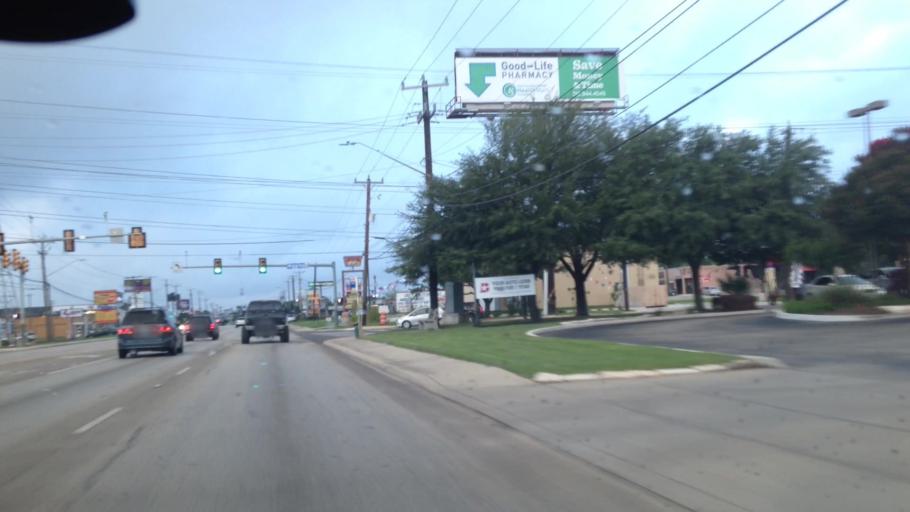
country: US
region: Texas
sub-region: Bexar County
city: Windcrest
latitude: 29.5637
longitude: -98.3908
